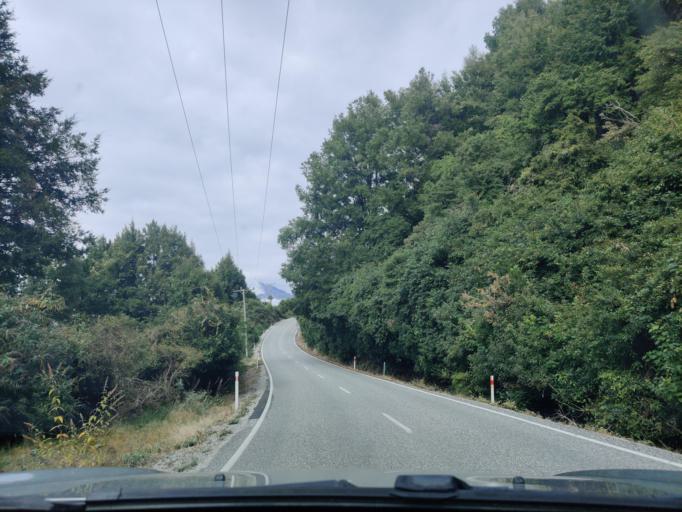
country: NZ
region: Otago
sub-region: Queenstown-Lakes District
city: Queenstown
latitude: -45.0731
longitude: 168.4963
